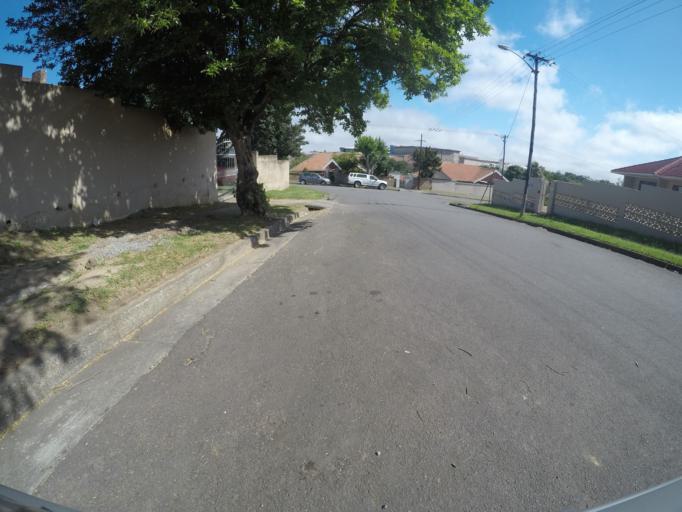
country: ZA
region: Eastern Cape
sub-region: Buffalo City Metropolitan Municipality
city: East London
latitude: -32.9813
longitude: 27.8931
